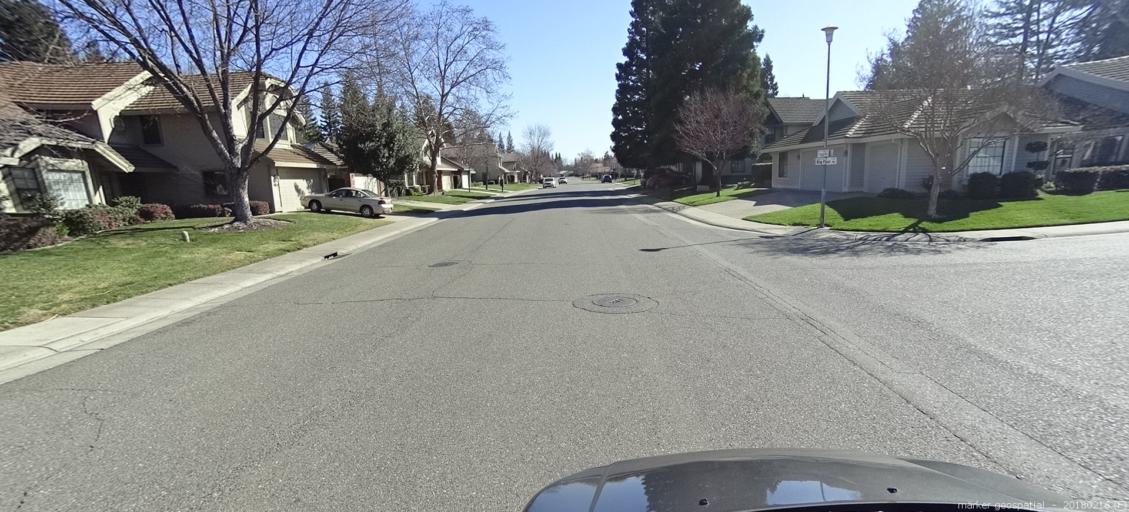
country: US
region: California
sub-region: Sacramento County
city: Gold River
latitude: 38.6229
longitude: -121.2475
